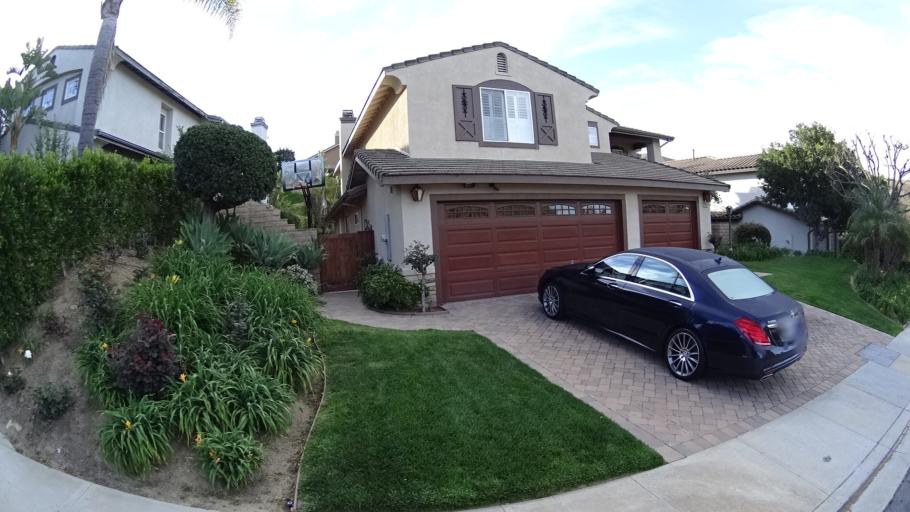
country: US
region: California
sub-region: Ventura County
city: Thousand Oaks
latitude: 34.2162
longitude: -118.8157
